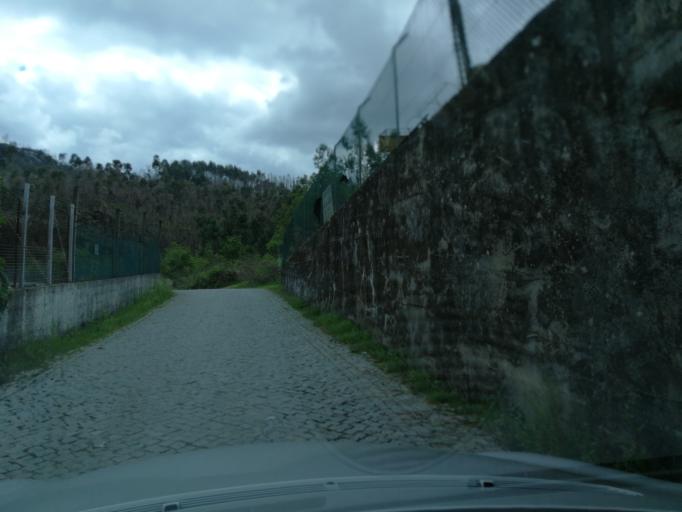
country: PT
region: Braga
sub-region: Braga
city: Braga
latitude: 41.5239
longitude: -8.4112
